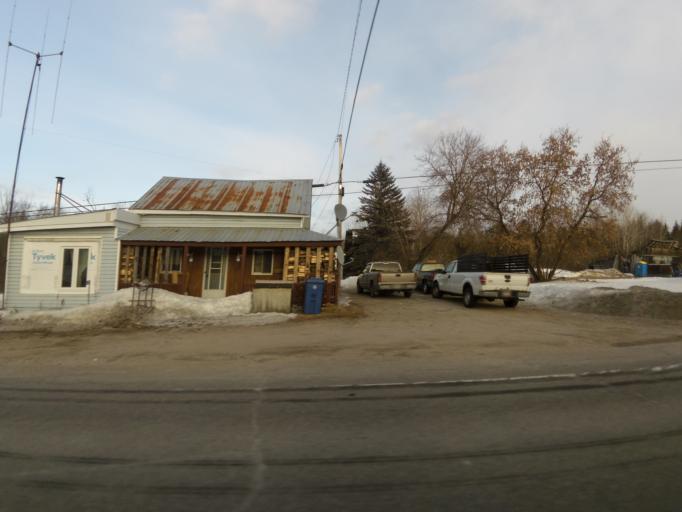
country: CA
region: Quebec
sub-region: Outaouais
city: Wakefield
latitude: 45.7840
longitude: -75.9506
